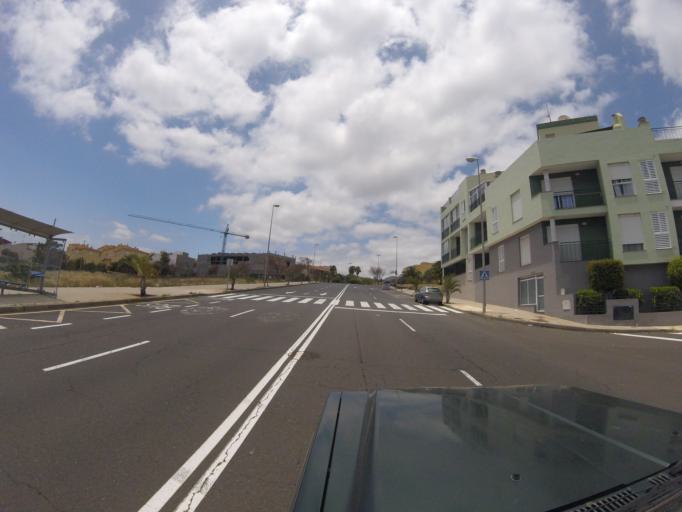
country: ES
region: Canary Islands
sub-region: Provincia de Santa Cruz de Tenerife
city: La Laguna
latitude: 28.4474
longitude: -16.3117
